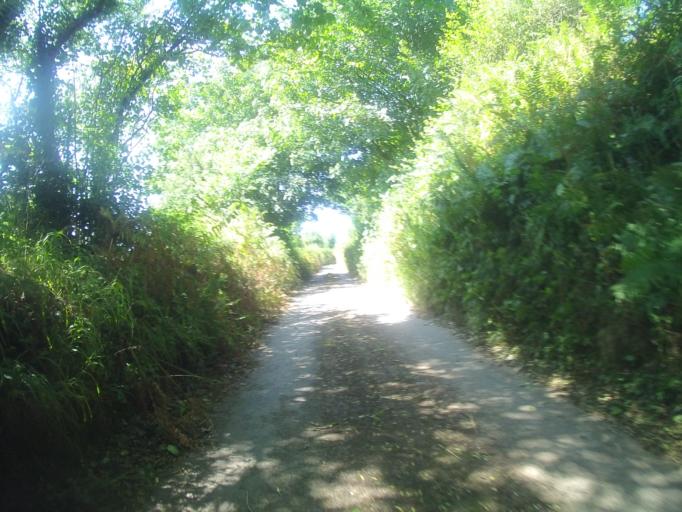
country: GB
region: England
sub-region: Devon
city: Dartmouth
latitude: 50.3631
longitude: -3.6218
